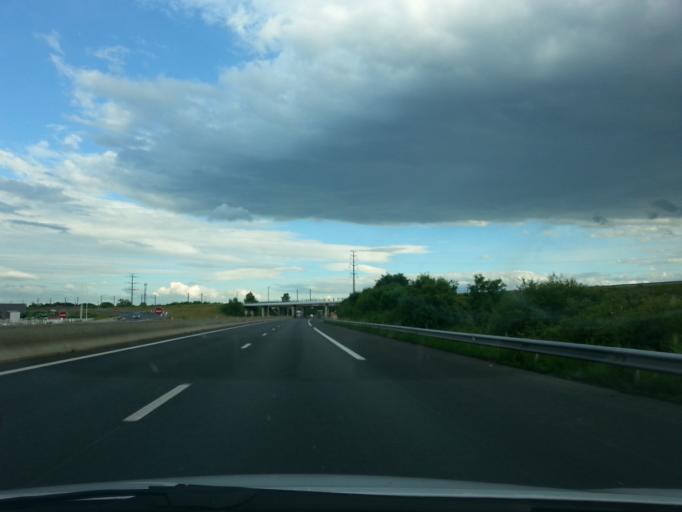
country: FR
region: Rhone-Alpes
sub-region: Departement du Rhone
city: Cailloux-sur-Fontaines
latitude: 45.8631
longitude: 4.9069
